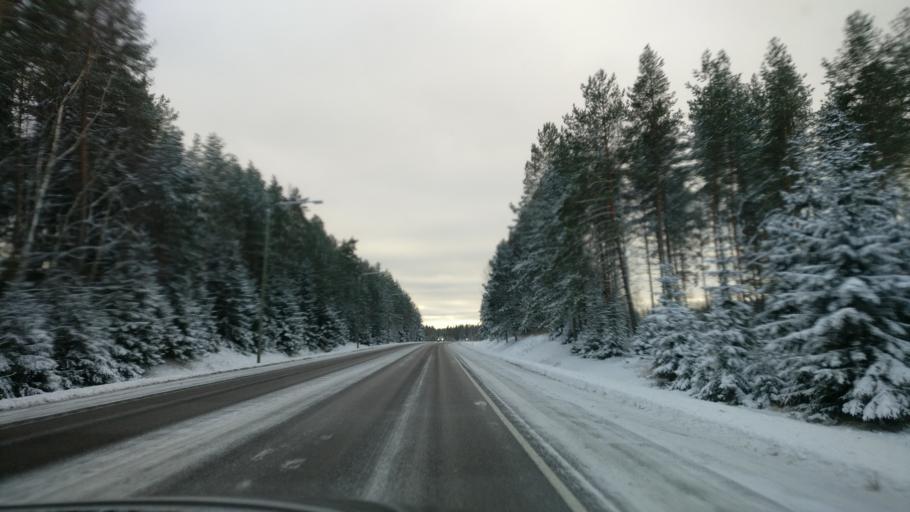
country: FI
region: Paijanne Tavastia
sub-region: Lahti
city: Heinola
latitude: 61.3274
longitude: 26.1588
